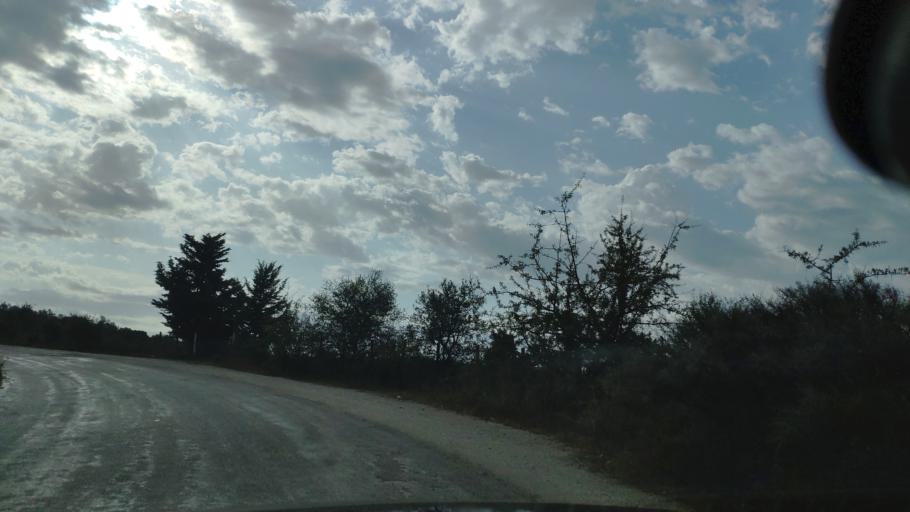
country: GR
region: West Greece
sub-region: Nomos Aitolias kai Akarnanias
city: Sardinia
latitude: 38.8876
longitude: 21.2160
